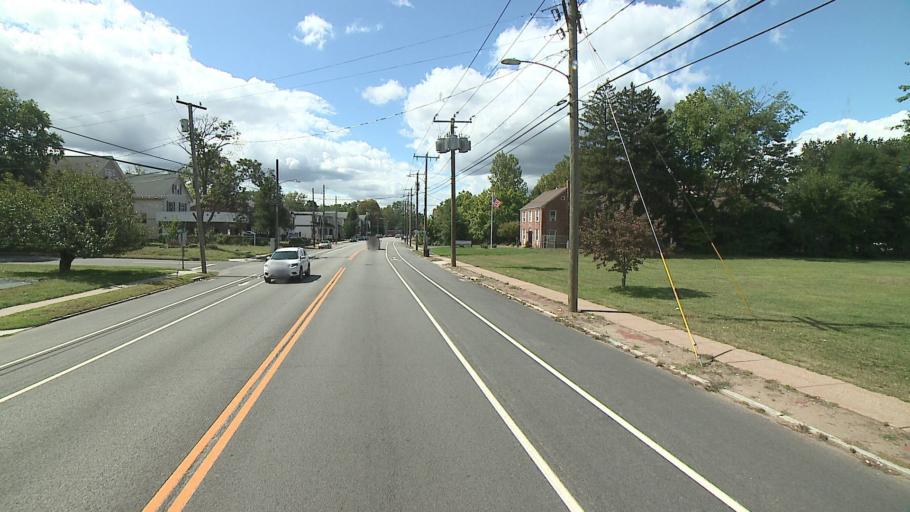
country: US
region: Connecticut
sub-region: Hartford County
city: East Hartford
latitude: 41.7785
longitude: -72.6153
